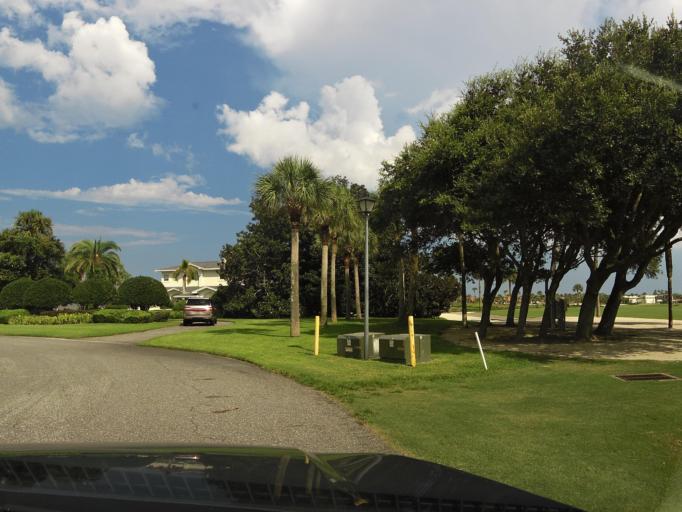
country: US
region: Florida
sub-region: Saint Johns County
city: Ponte Vedra Beach
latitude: 30.2476
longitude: -81.3834
